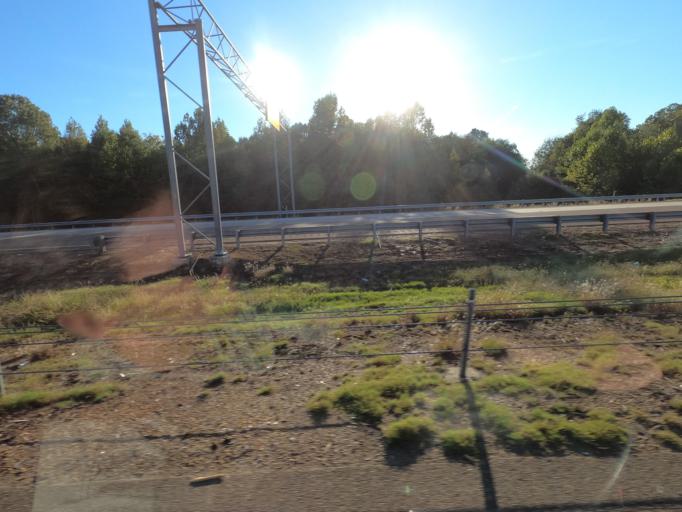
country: US
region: Tennessee
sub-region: Shelby County
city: Arlington
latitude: 35.2521
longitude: -89.6738
